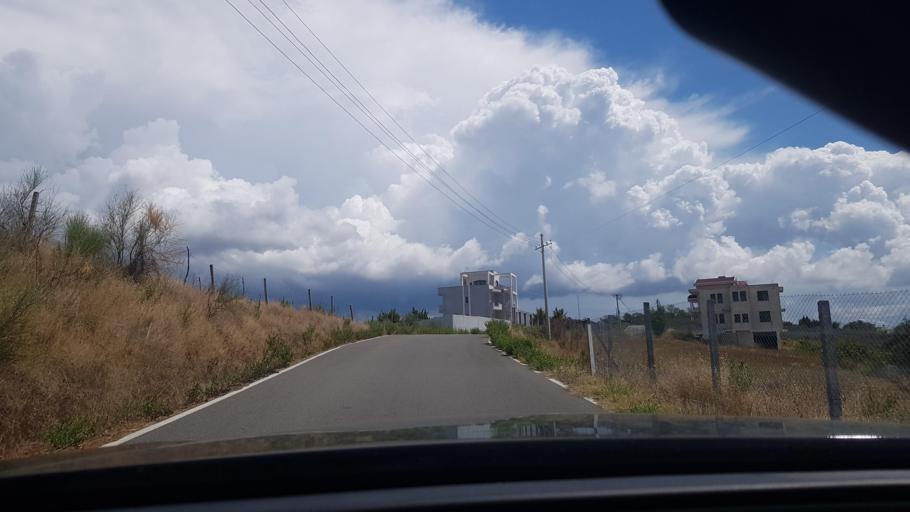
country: AL
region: Durres
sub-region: Rrethi i Durresit
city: Rrashbull
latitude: 41.2938
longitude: 19.5344
